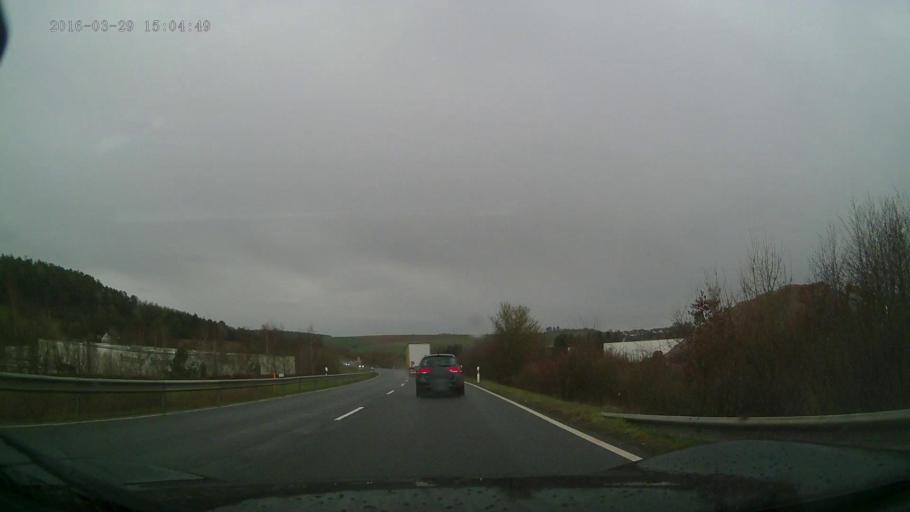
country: DE
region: Baden-Wuerttemberg
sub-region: Karlsruhe Region
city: Buchen
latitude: 49.5296
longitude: 9.3376
